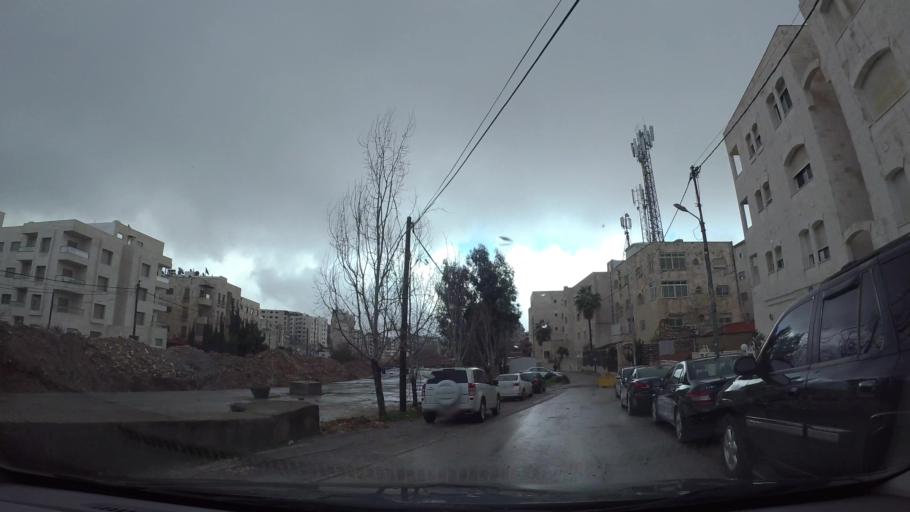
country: JO
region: Amman
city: Wadi as Sir
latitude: 31.9429
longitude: 35.8522
